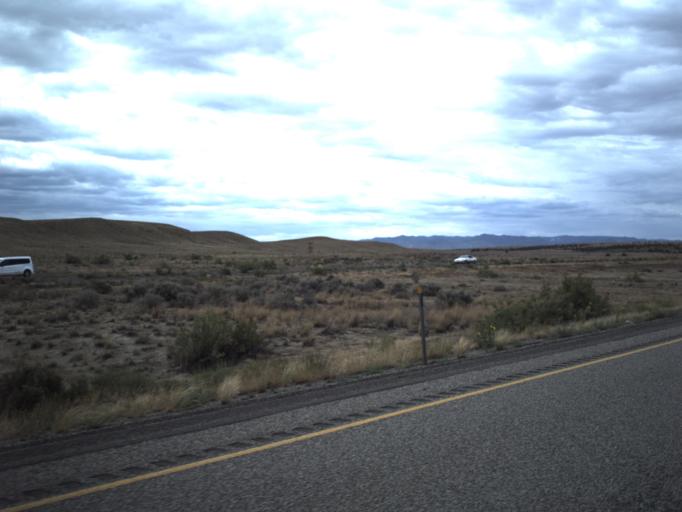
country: US
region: Colorado
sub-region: Mesa County
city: Loma
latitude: 39.1516
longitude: -109.1473
